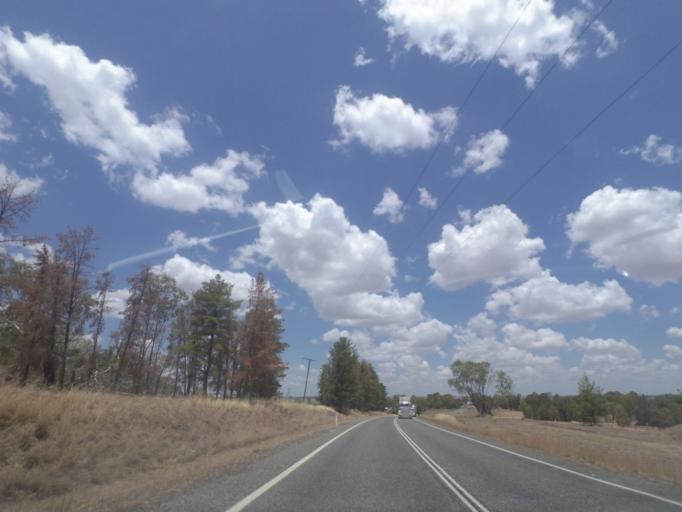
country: AU
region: Queensland
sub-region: Southern Downs
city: Warwick
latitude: -28.0293
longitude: 151.9865
